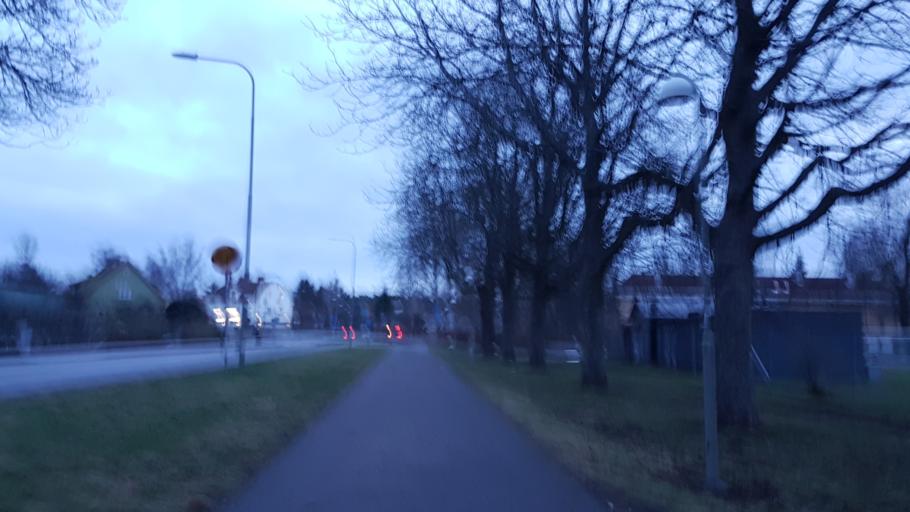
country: SE
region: Stockholm
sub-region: Stockholms Kommun
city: Arsta
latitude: 59.2805
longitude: 18.0493
